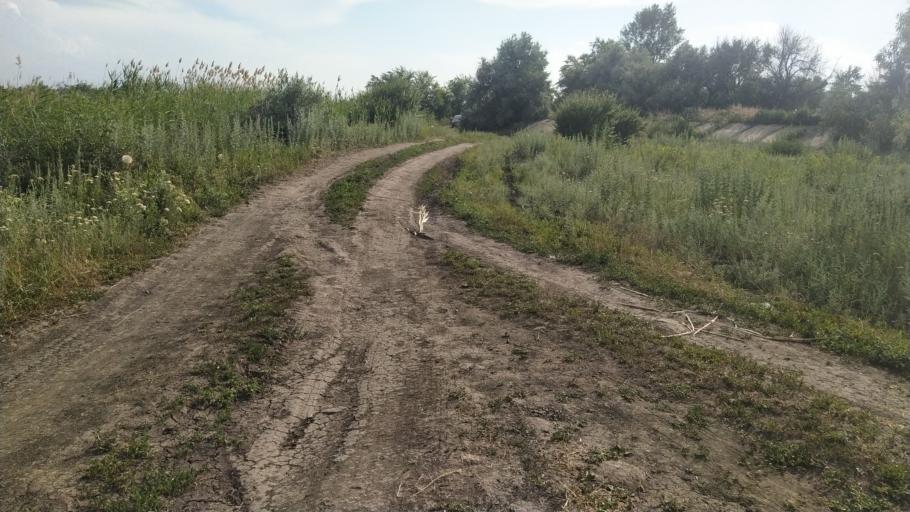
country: RU
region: Rostov
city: Kuleshovka
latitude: 47.1273
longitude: 39.6082
